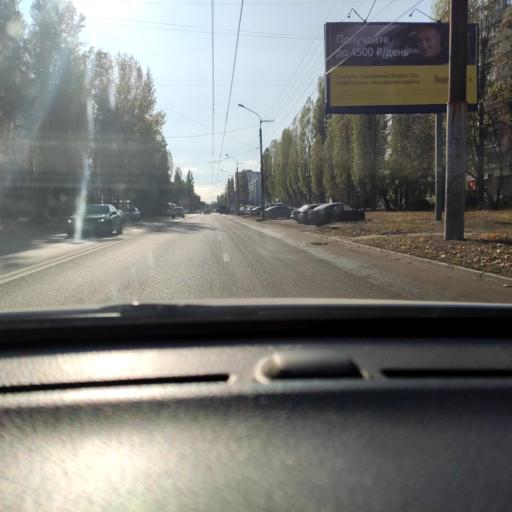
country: RU
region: Voronezj
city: Podgornoye
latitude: 51.7100
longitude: 39.1738
